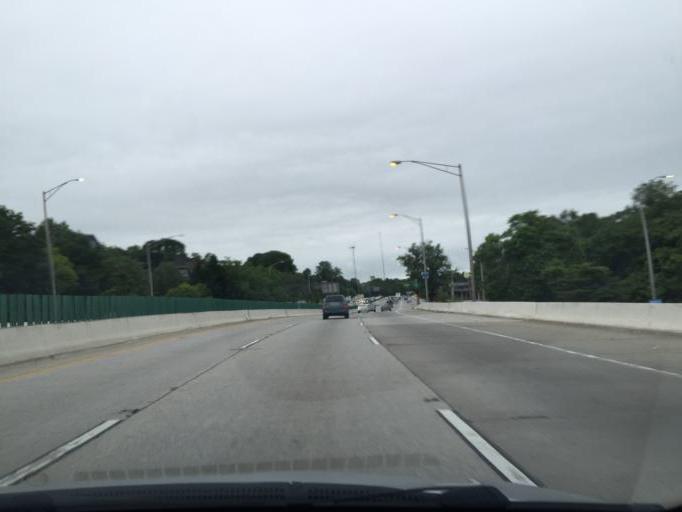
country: US
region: Maryland
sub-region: City of Baltimore
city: Baltimore
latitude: 39.3121
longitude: -76.6250
